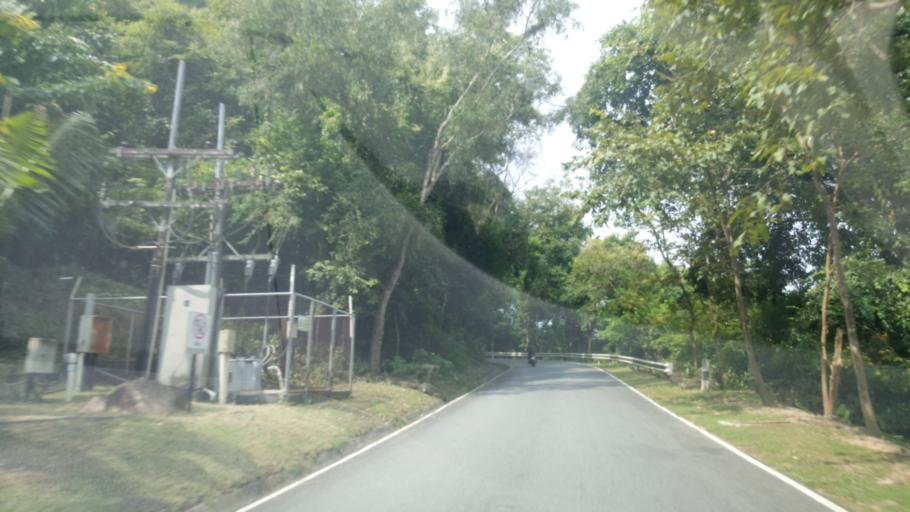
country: TH
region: Chon Buri
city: Ban Bueng
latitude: 13.2115
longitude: 101.0606
